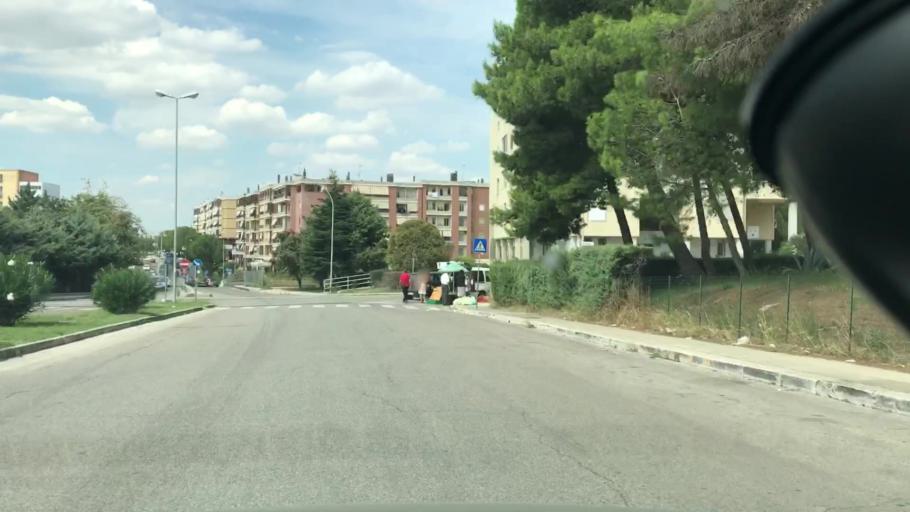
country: IT
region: Basilicate
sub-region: Provincia di Matera
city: Matera
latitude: 40.6763
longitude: 16.5833
